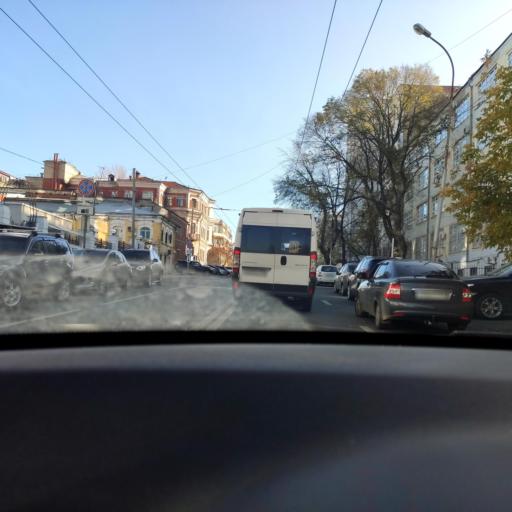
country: RU
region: Samara
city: Rozhdestveno
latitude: 53.1841
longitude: 50.0822
